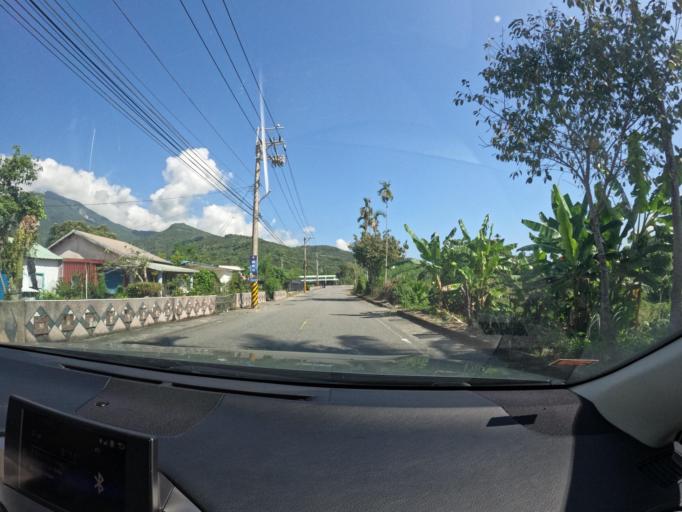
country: TW
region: Taiwan
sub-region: Hualien
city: Hualian
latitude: 23.5749
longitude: 121.3744
